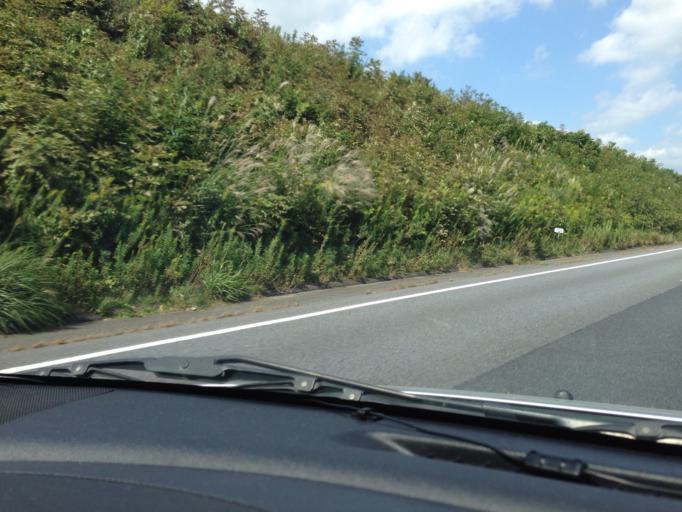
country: JP
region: Ibaraki
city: Tomobe
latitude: 36.3045
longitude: 140.3391
